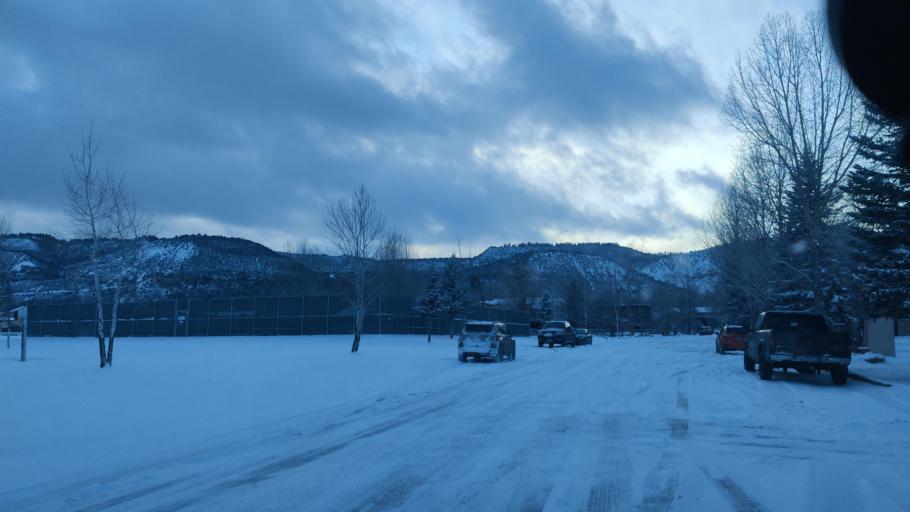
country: US
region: Colorado
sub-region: Ouray County
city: Ouray
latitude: 38.1487
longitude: -107.7549
